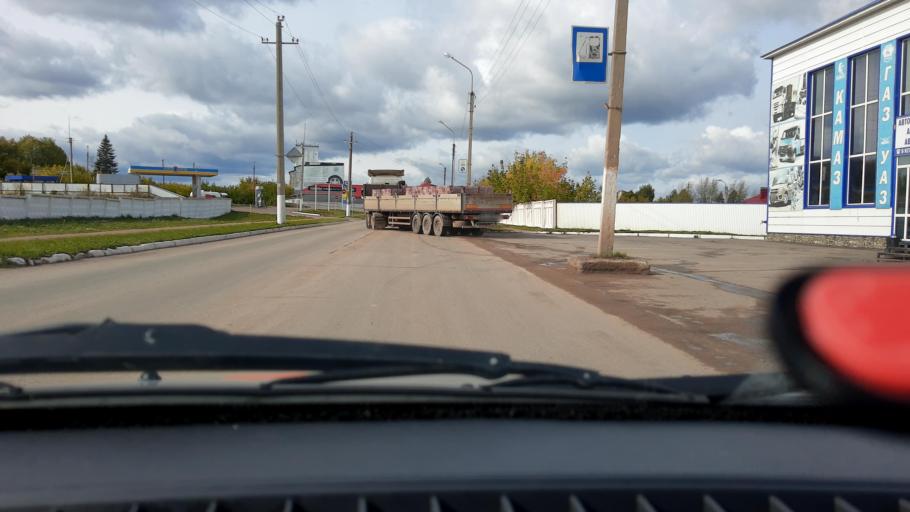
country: RU
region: Bashkortostan
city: Belebey
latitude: 54.0967
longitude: 54.1251
